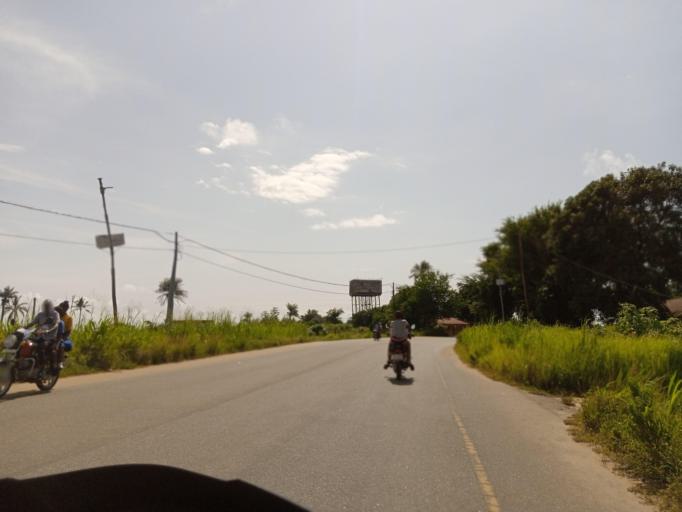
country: SL
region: Northern Province
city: Tintafor
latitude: 8.6179
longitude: -13.2097
